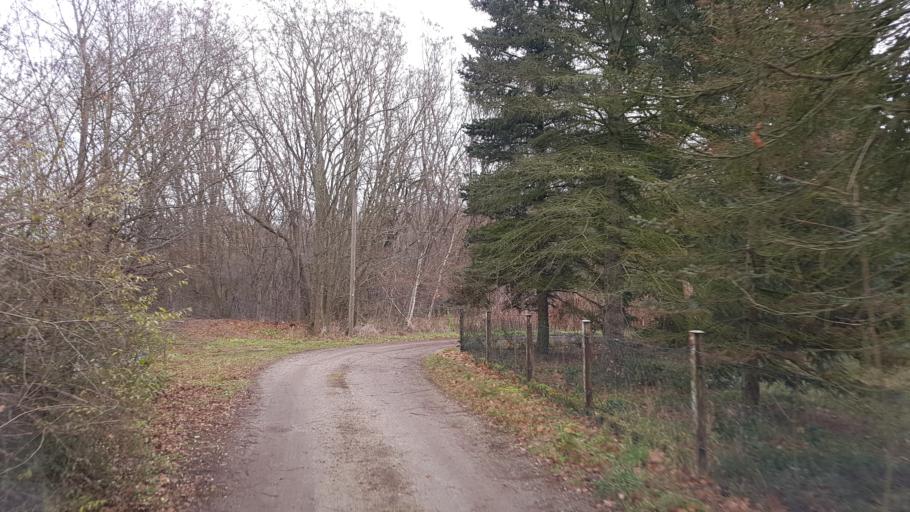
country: DE
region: Brandenburg
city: Sallgast
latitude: 51.5875
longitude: 13.8221
